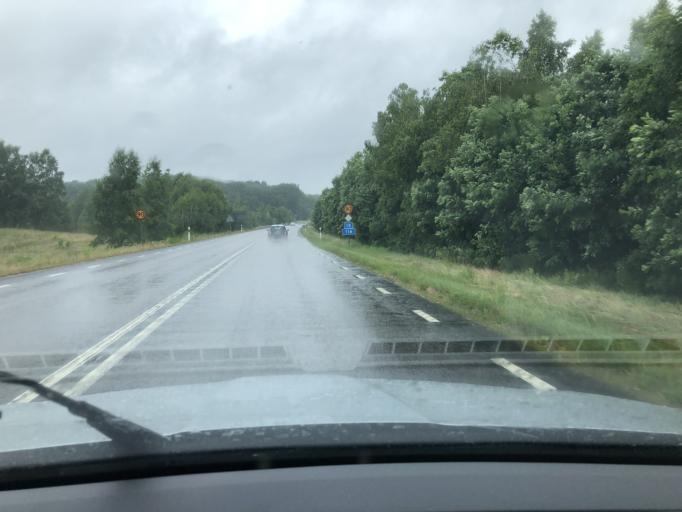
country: SE
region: Blekinge
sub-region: Olofstroms Kommun
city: Jamshog
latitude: 56.2401
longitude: 14.5396
